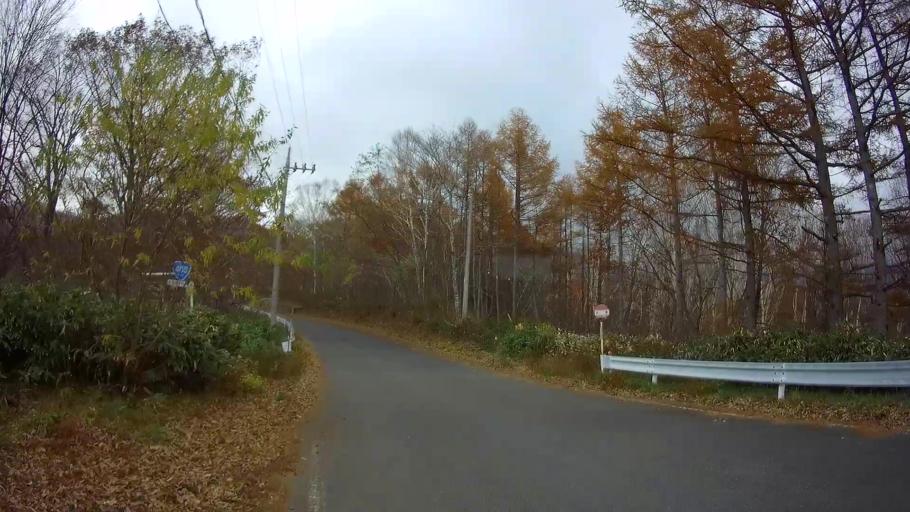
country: JP
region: Gunma
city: Nakanojomachi
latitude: 36.6831
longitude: 138.6595
